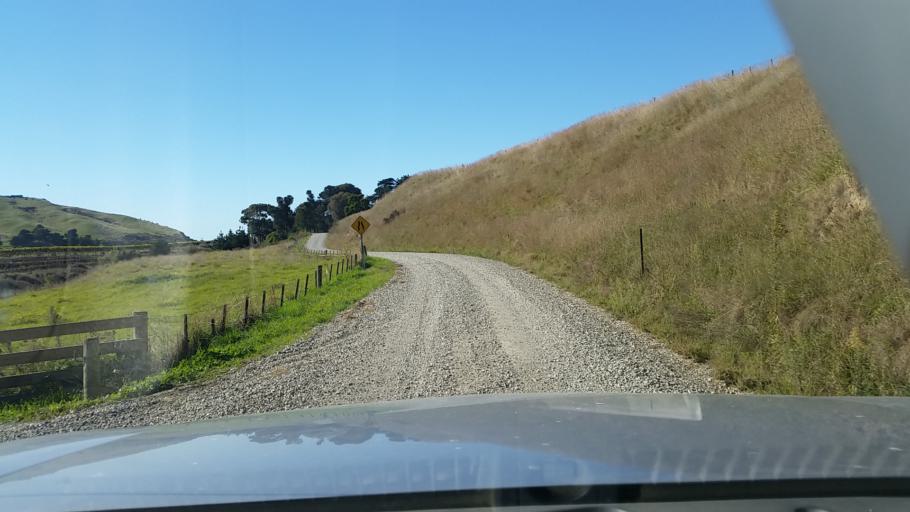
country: NZ
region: Marlborough
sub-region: Marlborough District
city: Blenheim
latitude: -41.6683
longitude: 174.1496
